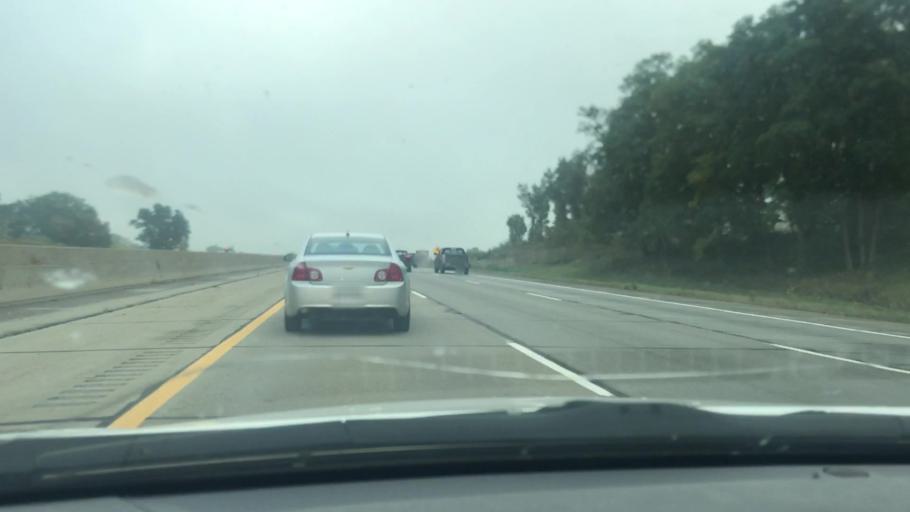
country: US
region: Michigan
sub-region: Livingston County
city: Howell
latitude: 42.5802
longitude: -83.8938
